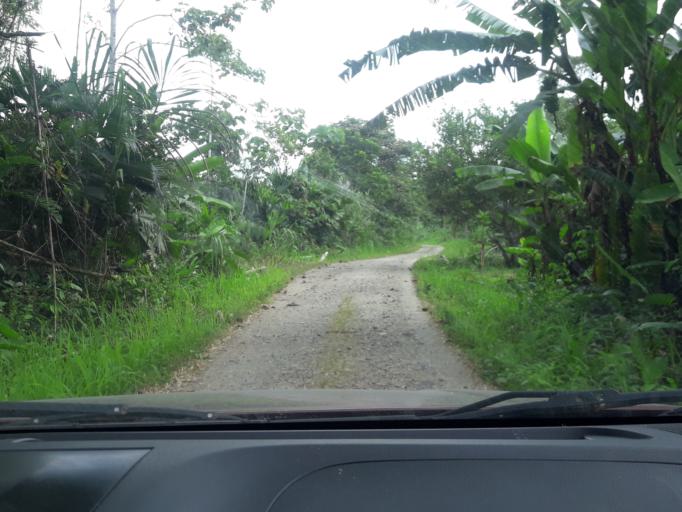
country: EC
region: Napo
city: Tena
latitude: -1.0964
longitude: -77.6777
